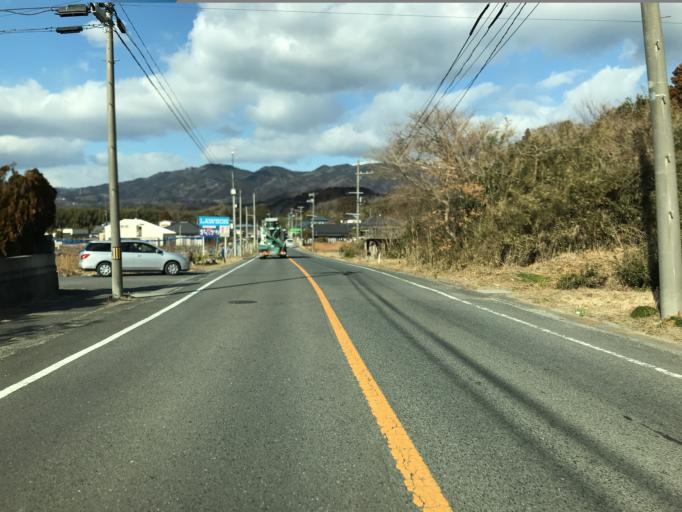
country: JP
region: Fukushima
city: Iwaki
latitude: 37.1160
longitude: 140.8708
